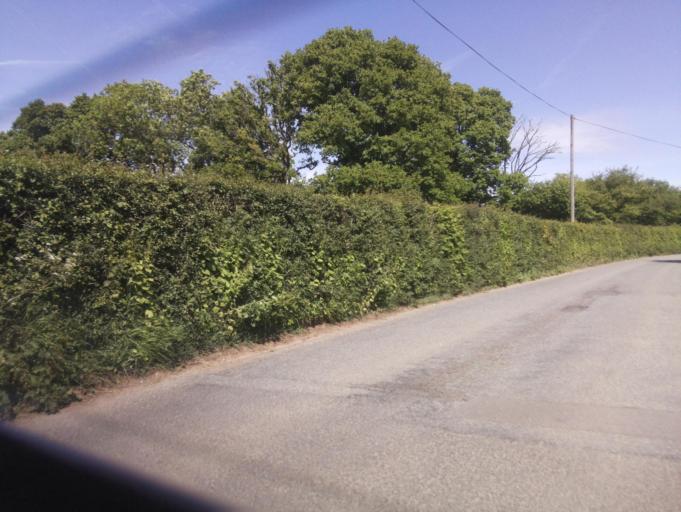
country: GB
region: England
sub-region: Devon
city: Ottery St Mary
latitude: 50.7629
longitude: -3.2681
